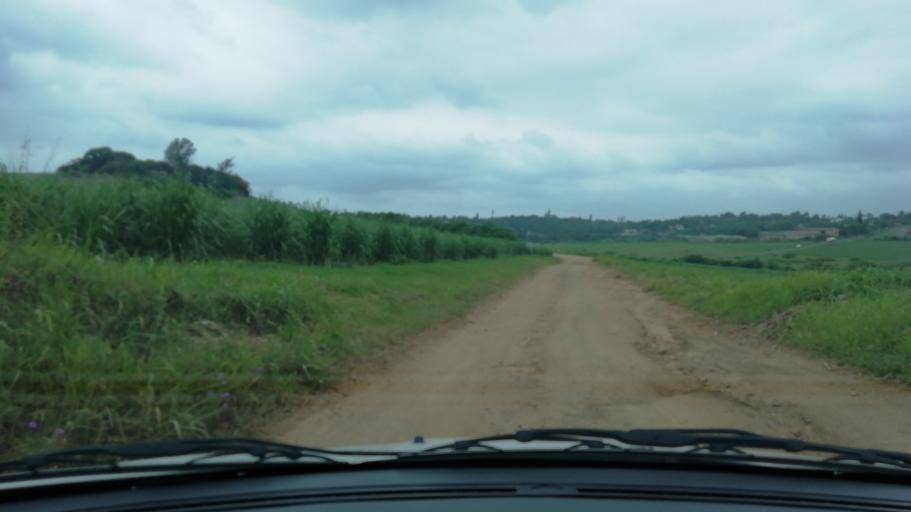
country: ZA
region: KwaZulu-Natal
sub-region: uThungulu District Municipality
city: Empangeni
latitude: -28.7350
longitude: 31.9079
